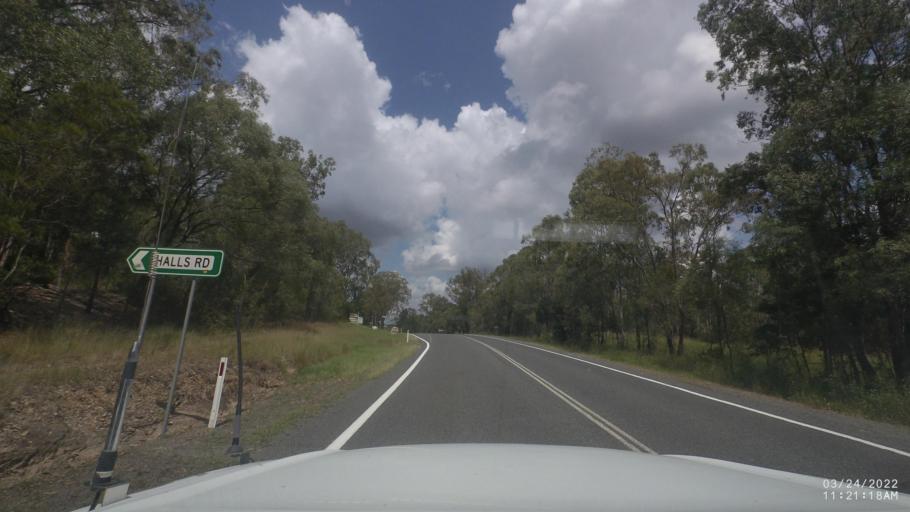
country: AU
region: Queensland
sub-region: Logan
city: Windaroo
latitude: -27.7991
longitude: 153.1771
